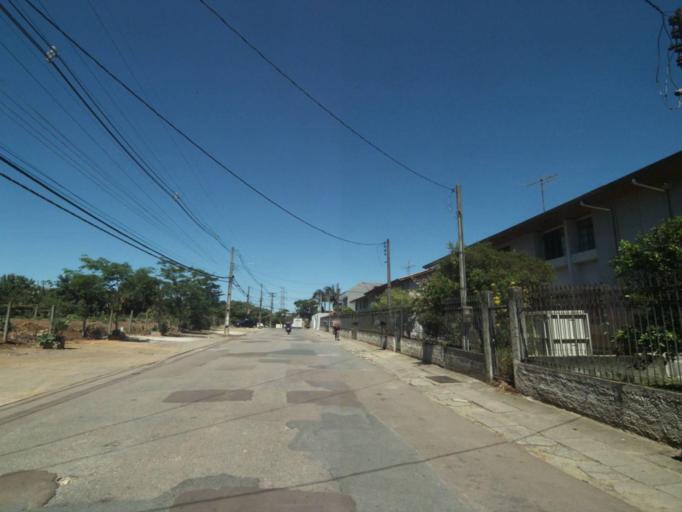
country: BR
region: Parana
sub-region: Curitiba
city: Curitiba
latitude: -25.4753
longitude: -49.3384
